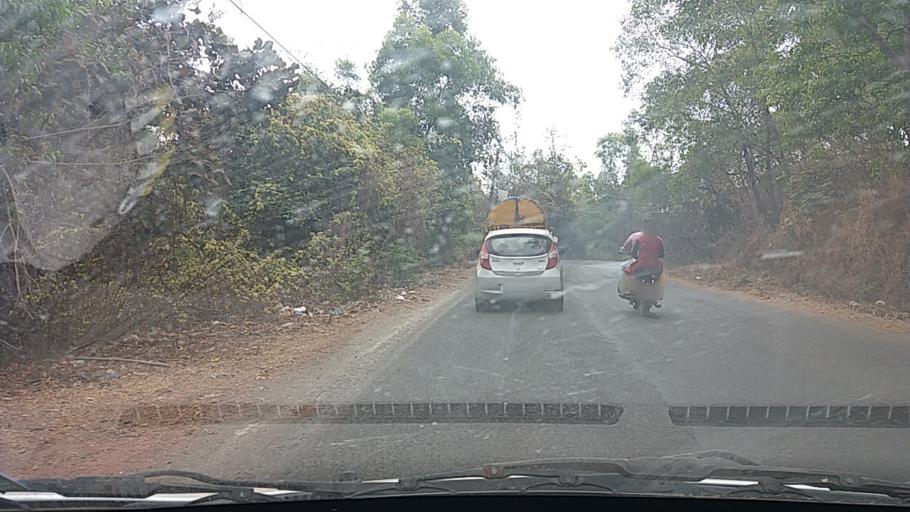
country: IN
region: Goa
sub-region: North Goa
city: Saligao
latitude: 15.5393
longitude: 73.7931
